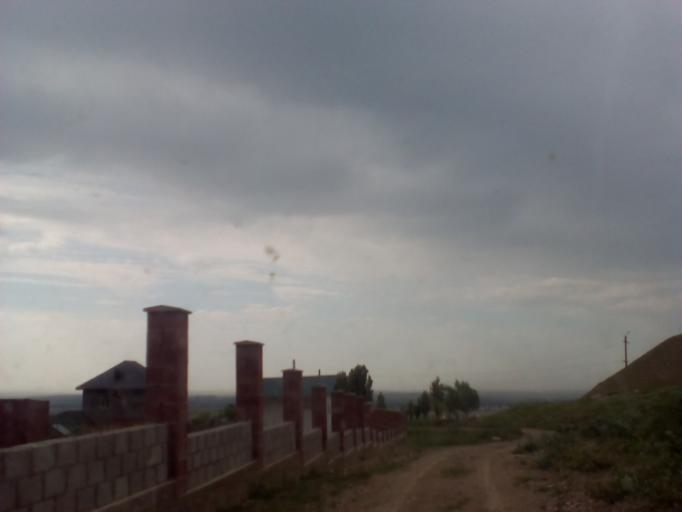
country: KZ
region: Almaty Oblysy
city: Burunday
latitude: 43.1487
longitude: 76.3858
